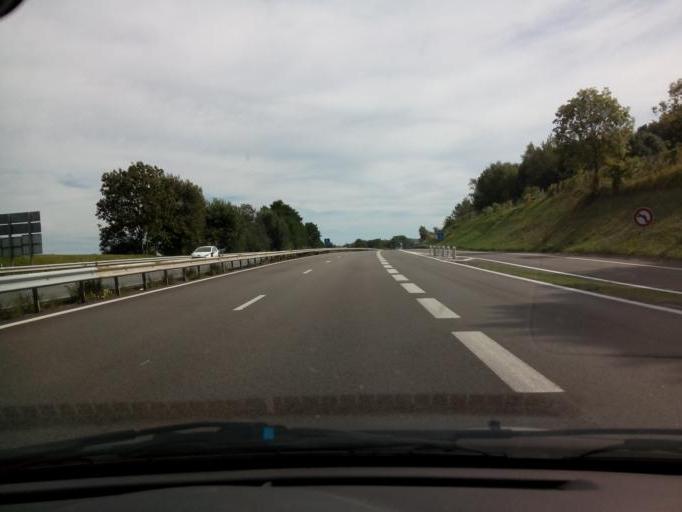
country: FR
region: Rhone-Alpes
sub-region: Departement de l'Isere
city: Saint-Victor-de-Cessieu
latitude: 45.5295
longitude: 5.4093
